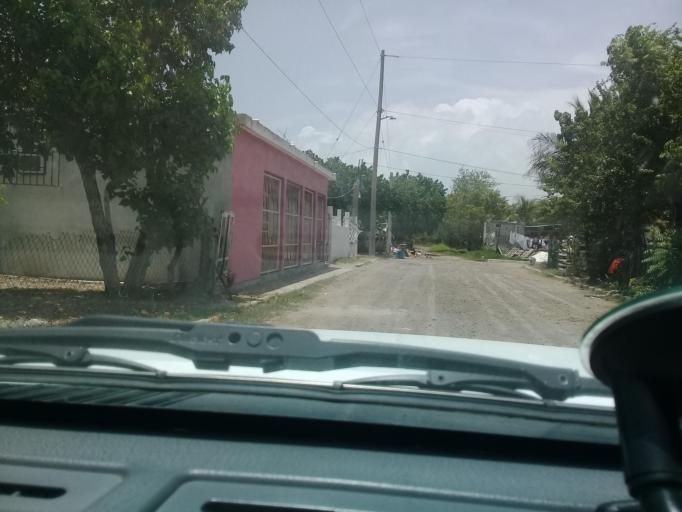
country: MX
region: Tamaulipas
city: Ciudad Madero
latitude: 22.2316
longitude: -97.8172
